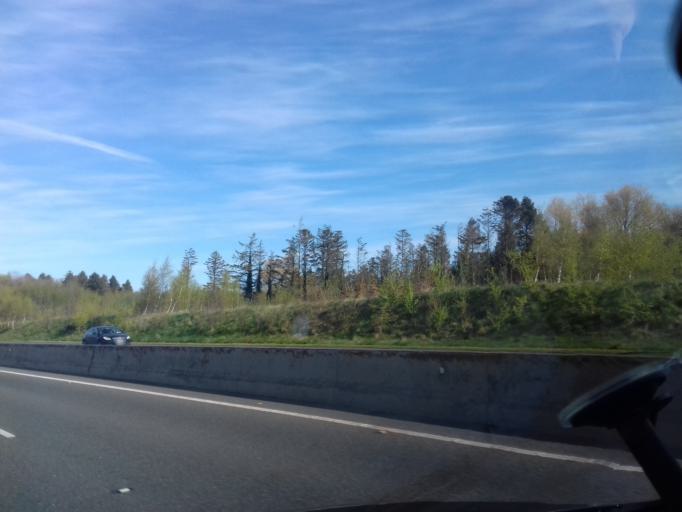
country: IE
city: Kentstown
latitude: 53.5968
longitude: -6.5912
